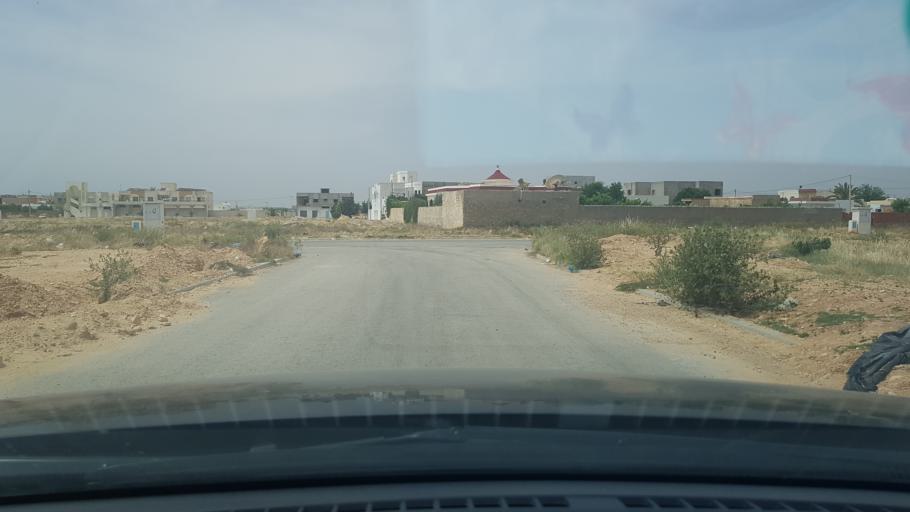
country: TN
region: Safaqis
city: Al Qarmadah
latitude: 34.8228
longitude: 10.7428
